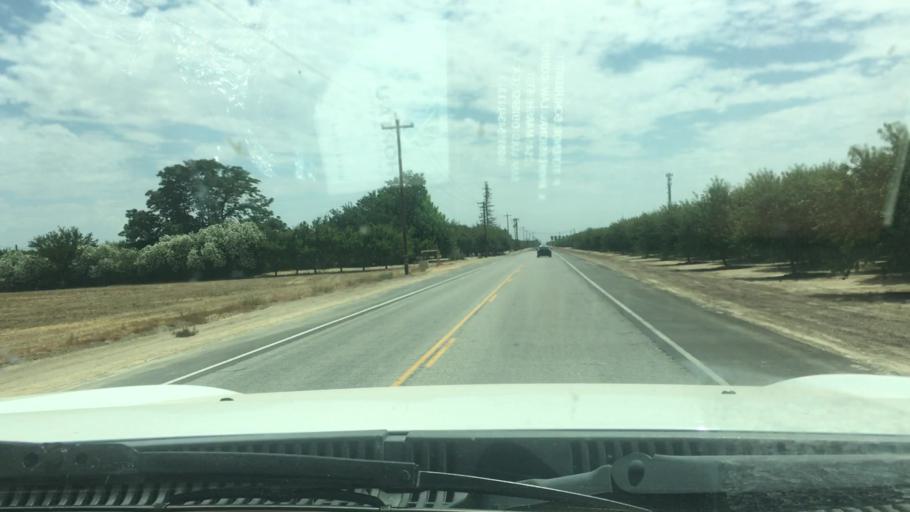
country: US
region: California
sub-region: Kern County
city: Wasco
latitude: 35.5579
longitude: -119.3581
